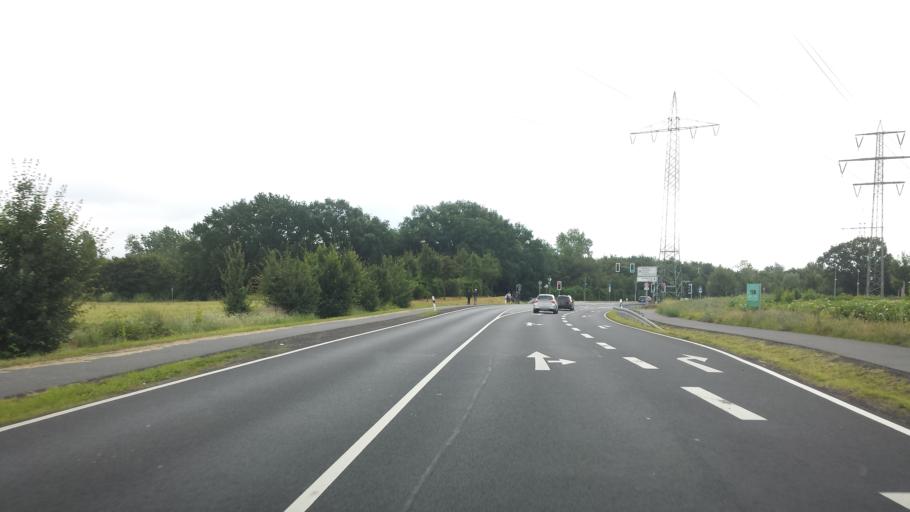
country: DE
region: Hesse
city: Kelsterbach
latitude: 50.0922
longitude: 8.5513
